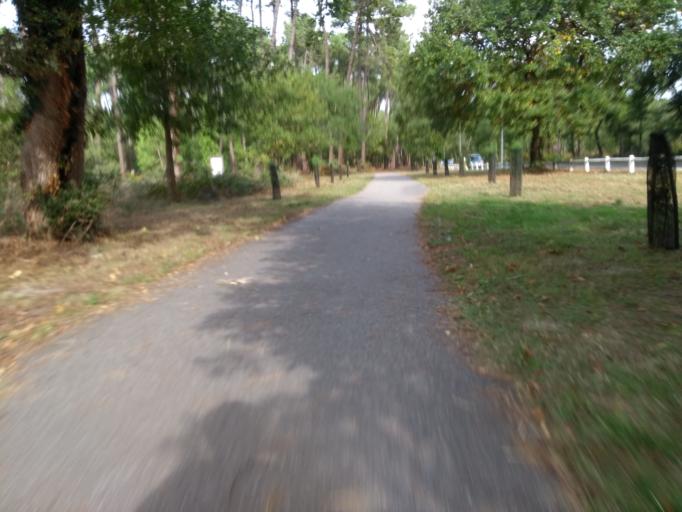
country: FR
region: Aquitaine
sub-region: Departement de la Gironde
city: Canejan
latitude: 44.7533
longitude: -0.6521
